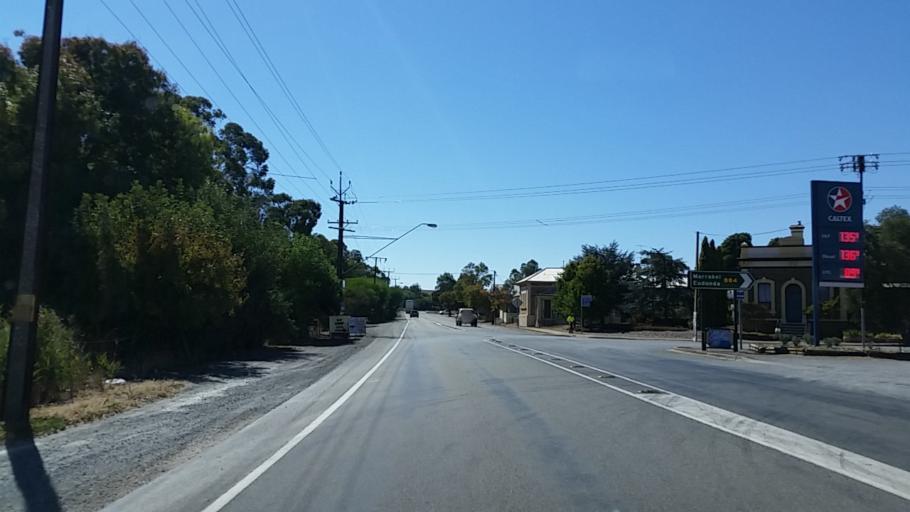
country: AU
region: South Australia
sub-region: Light
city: Kapunda
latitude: -34.0833
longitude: 138.7801
